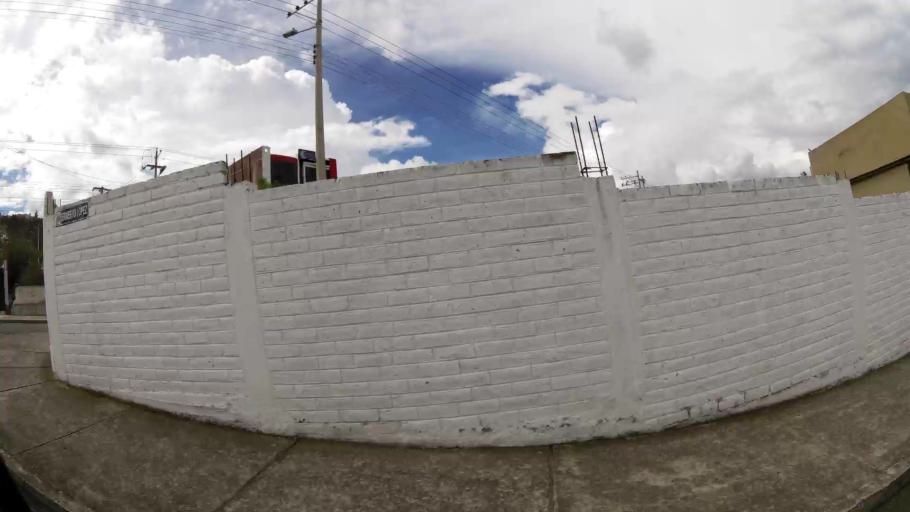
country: EC
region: Tungurahua
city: Ambato
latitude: -1.2749
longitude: -78.6395
